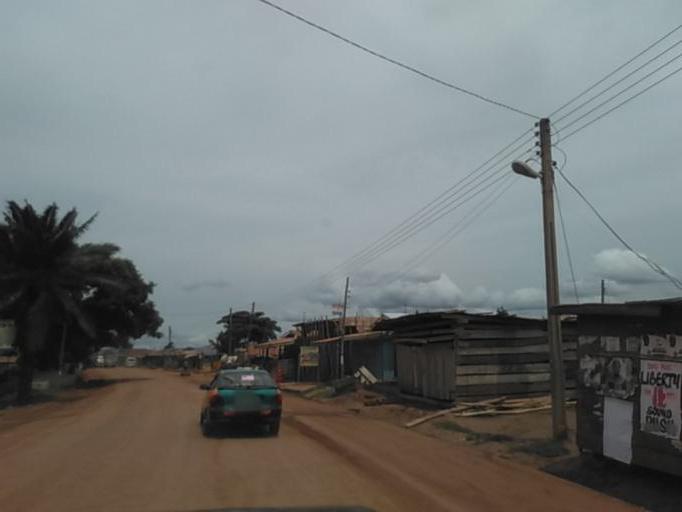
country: GH
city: Akropong
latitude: 6.1336
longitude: 0.0028
